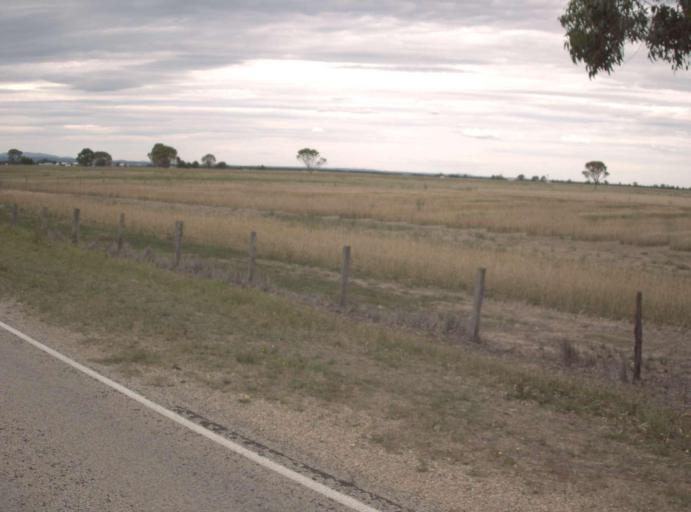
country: AU
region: Victoria
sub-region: East Gippsland
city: Bairnsdale
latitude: -37.8929
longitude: 147.5560
